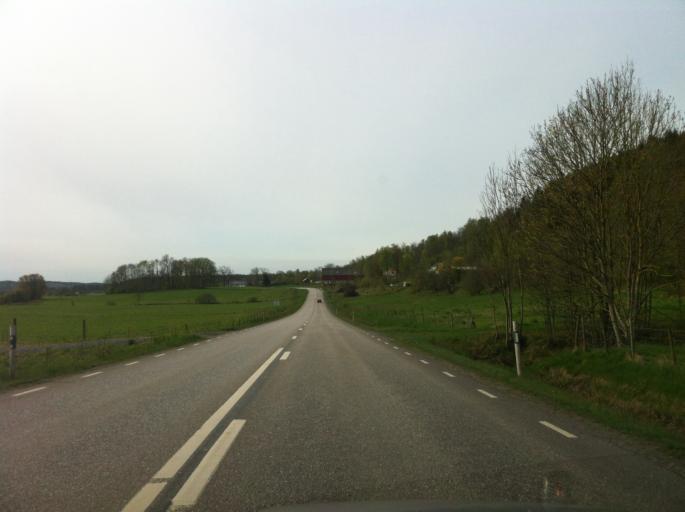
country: SE
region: Vaestra Goetaland
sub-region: Harryda Kommun
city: Ravlanda
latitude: 57.5426
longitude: 12.5334
